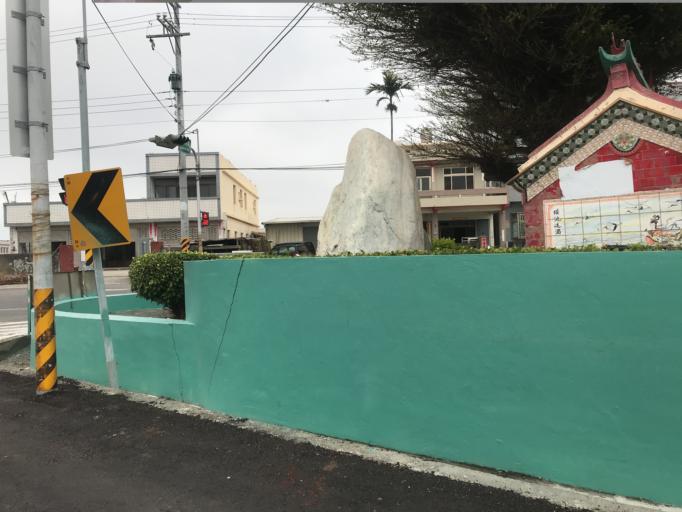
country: TW
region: Taiwan
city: Fengyuan
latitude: 24.3748
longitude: 120.5976
